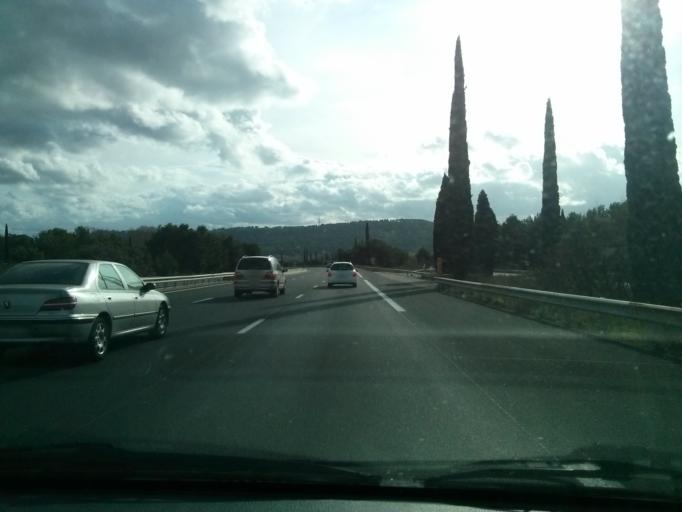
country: FR
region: Provence-Alpes-Cote d'Azur
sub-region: Departement des Bouches-du-Rhone
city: Coudoux
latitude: 43.5573
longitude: 5.2300
